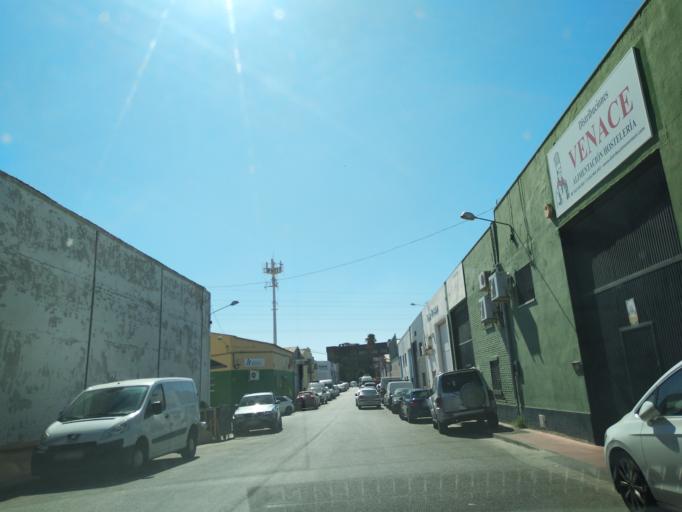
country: ES
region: Andalusia
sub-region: Provincia de Malaga
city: Malaga
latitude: 36.7134
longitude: -4.4873
